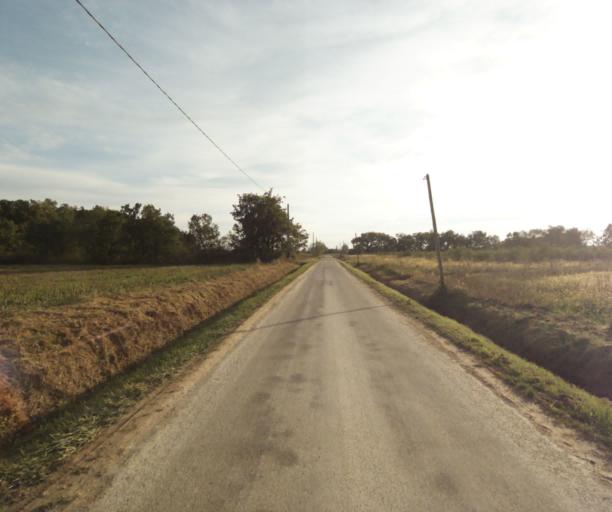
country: FR
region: Midi-Pyrenees
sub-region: Departement du Tarn-et-Garonne
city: Labastide-Saint-Pierre
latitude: 43.8930
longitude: 1.3568
